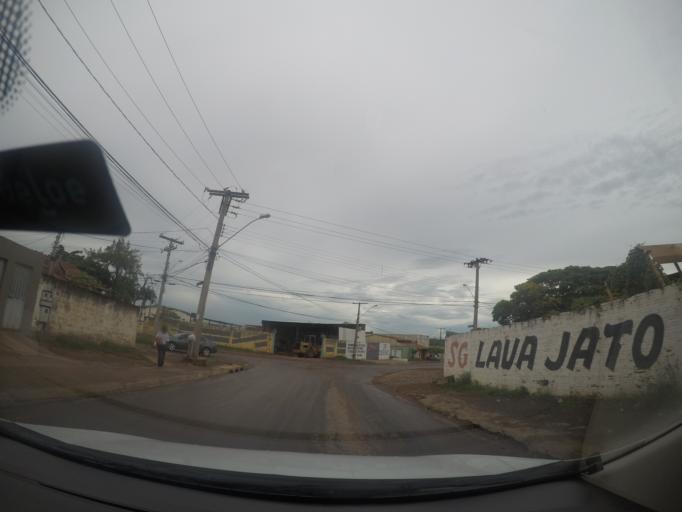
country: BR
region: Goias
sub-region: Goiania
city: Goiania
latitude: -16.6311
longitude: -49.2358
